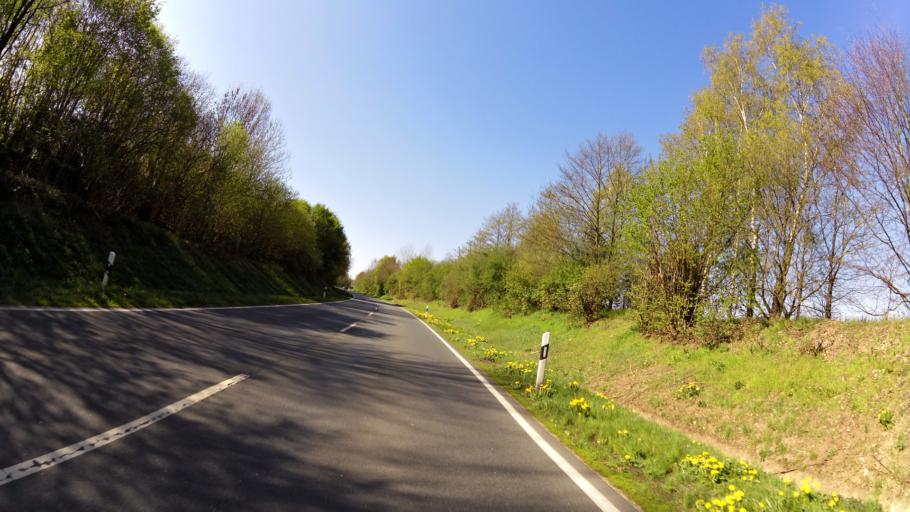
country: DE
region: Lower Saxony
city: Syke
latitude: 52.9243
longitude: 8.8074
